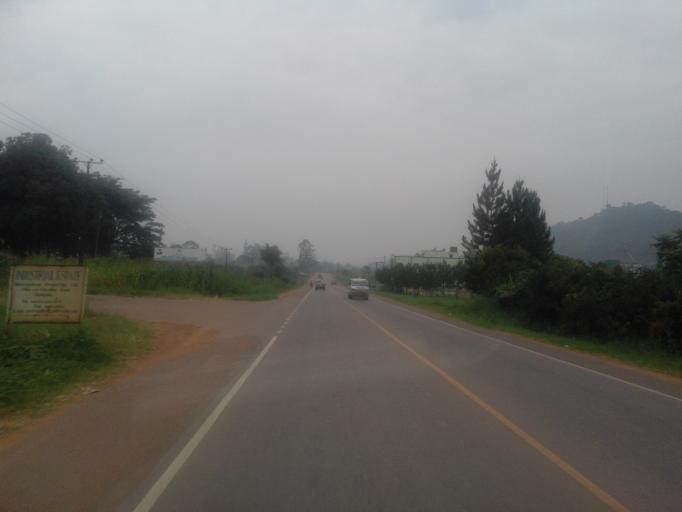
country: UG
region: Central Region
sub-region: Mukono District
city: Mukono
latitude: 0.3551
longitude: 32.7912
